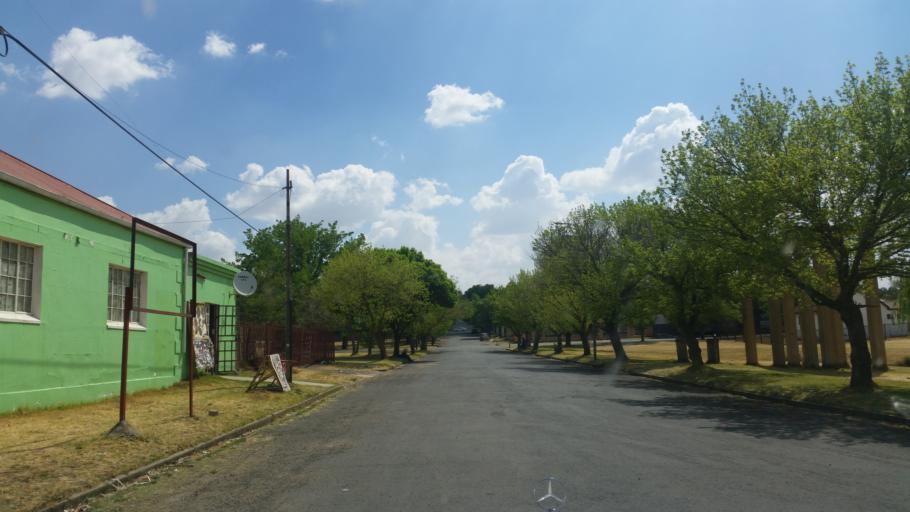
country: ZA
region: Orange Free State
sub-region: Thabo Mofutsanyana District Municipality
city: Reitz
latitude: -27.8036
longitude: 28.4301
